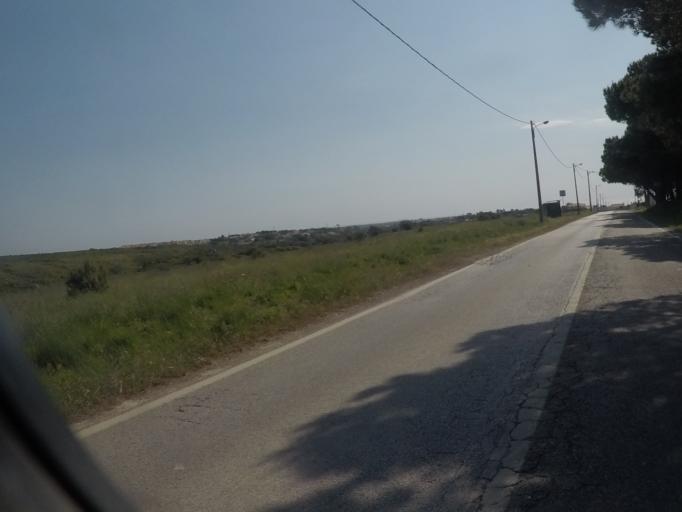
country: PT
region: Setubal
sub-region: Sesimbra
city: Sesimbra
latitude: 38.4459
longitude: -9.1604
